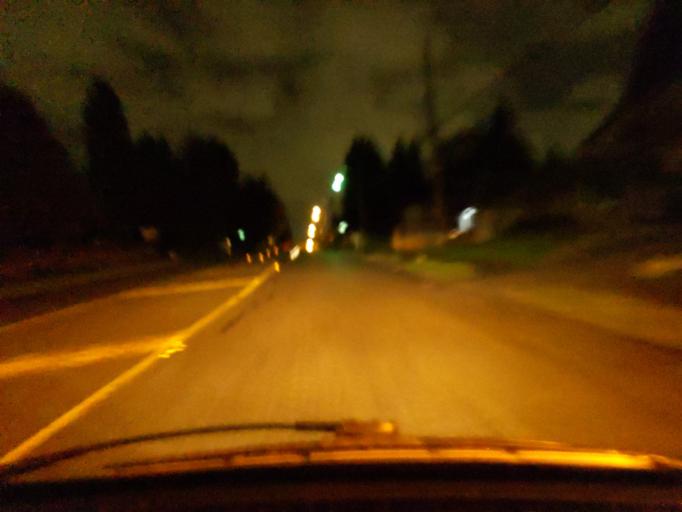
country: CA
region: British Columbia
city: New Westminster
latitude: 49.1990
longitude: -122.8660
